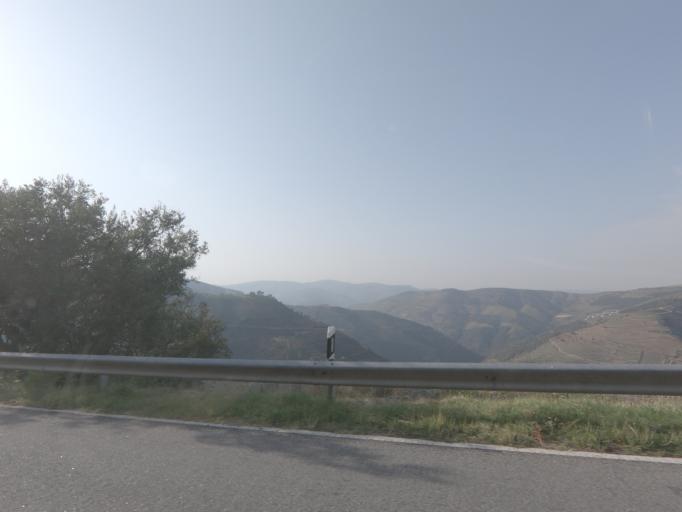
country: PT
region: Viseu
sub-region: Tabuaco
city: Tabuaco
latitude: 41.1198
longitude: -7.5629
